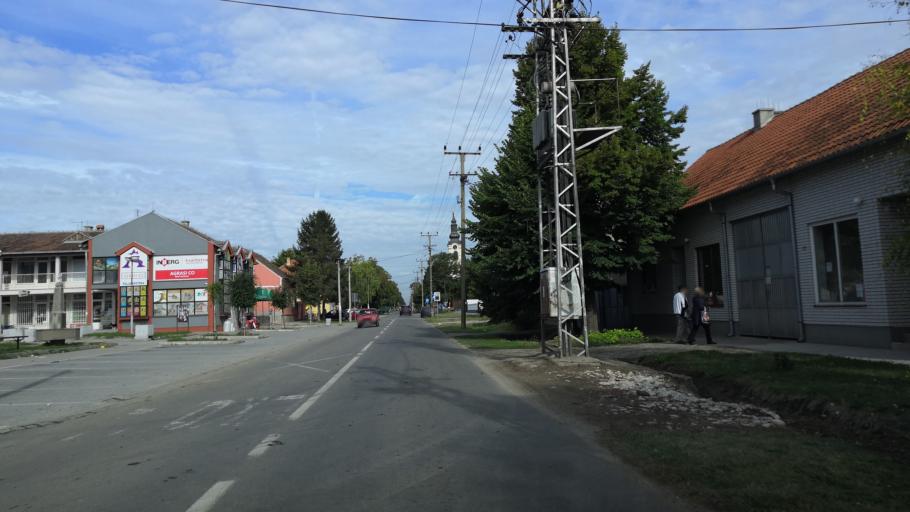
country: RS
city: Novi Karlovci
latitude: 45.0787
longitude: 20.1789
